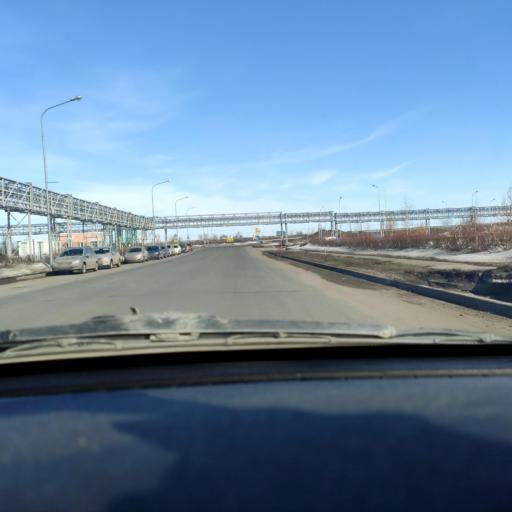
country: RU
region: Samara
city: Podstepki
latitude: 53.5595
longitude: 49.1846
